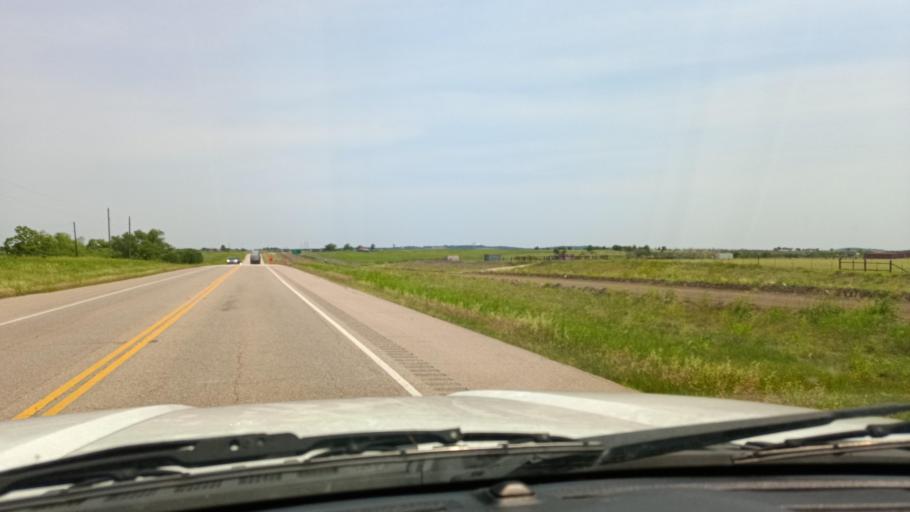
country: US
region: Texas
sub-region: Bell County
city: Little River-Academy
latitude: 30.9900
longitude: -97.2821
